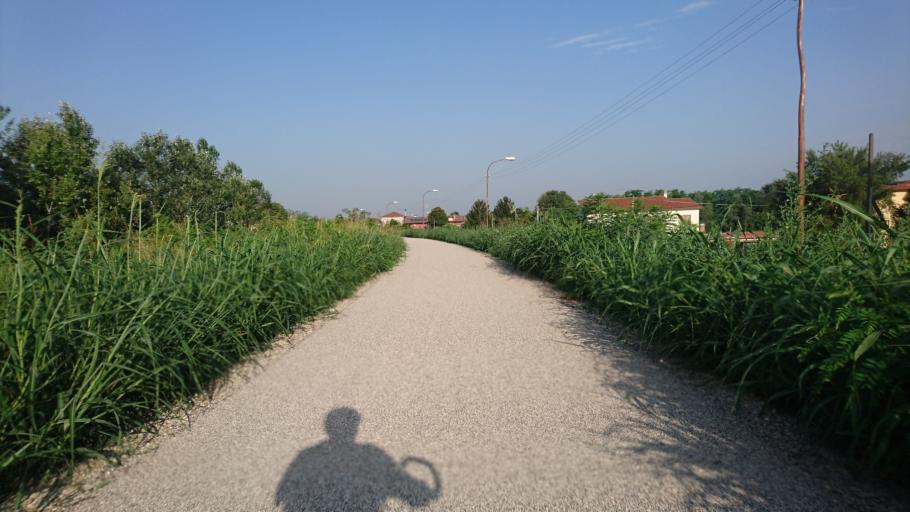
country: IT
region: Veneto
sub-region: Provincia di Padova
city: Cadoneghe
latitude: 45.4378
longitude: 11.9352
